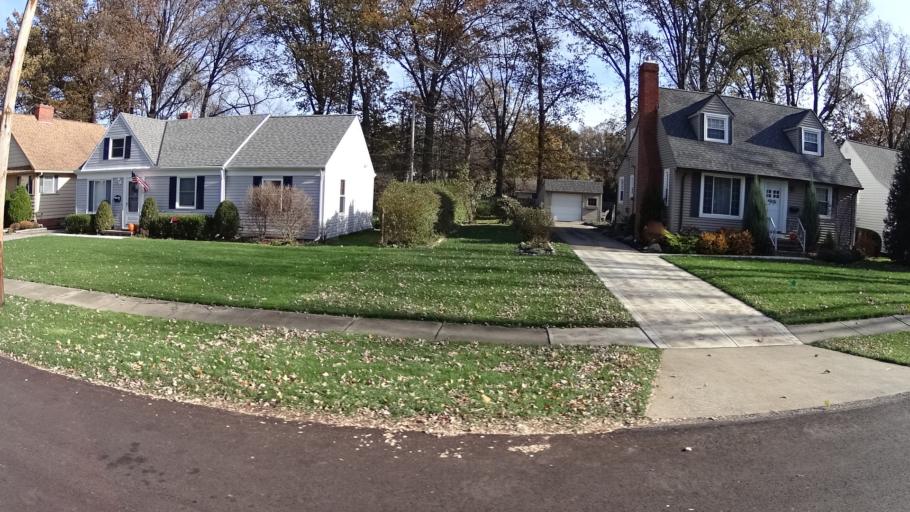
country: US
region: Ohio
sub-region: Lorain County
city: Avon Lake
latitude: 41.5080
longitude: -81.9950
